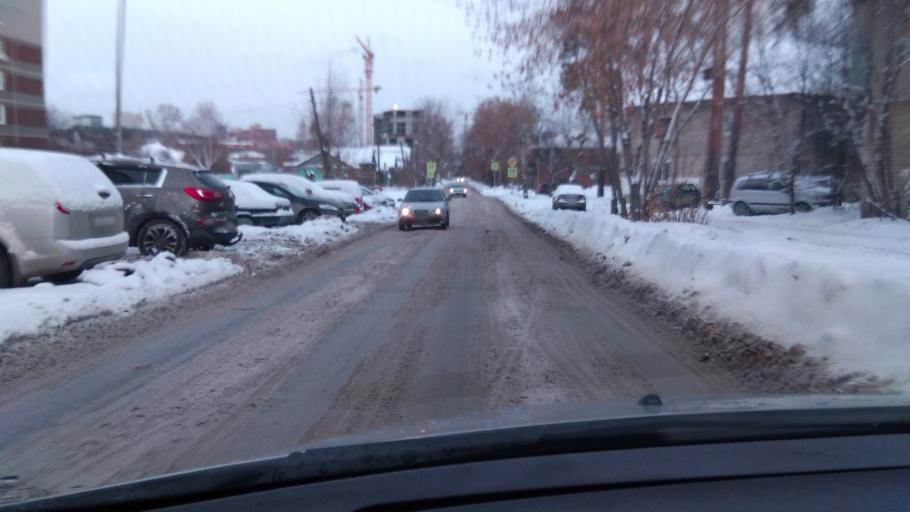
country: RU
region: Sverdlovsk
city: Sovkhoznyy
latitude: 56.8181
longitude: 60.5461
